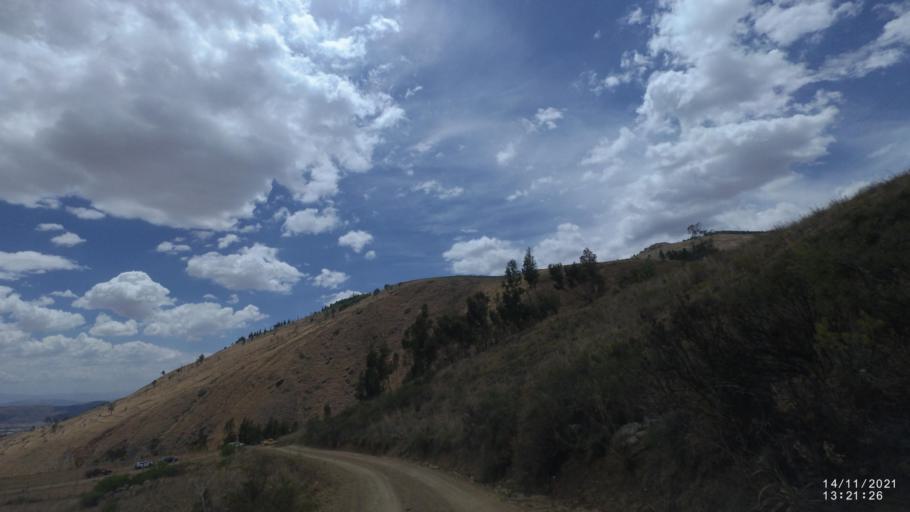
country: BO
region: Cochabamba
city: Colomi
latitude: -17.3754
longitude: -65.9829
